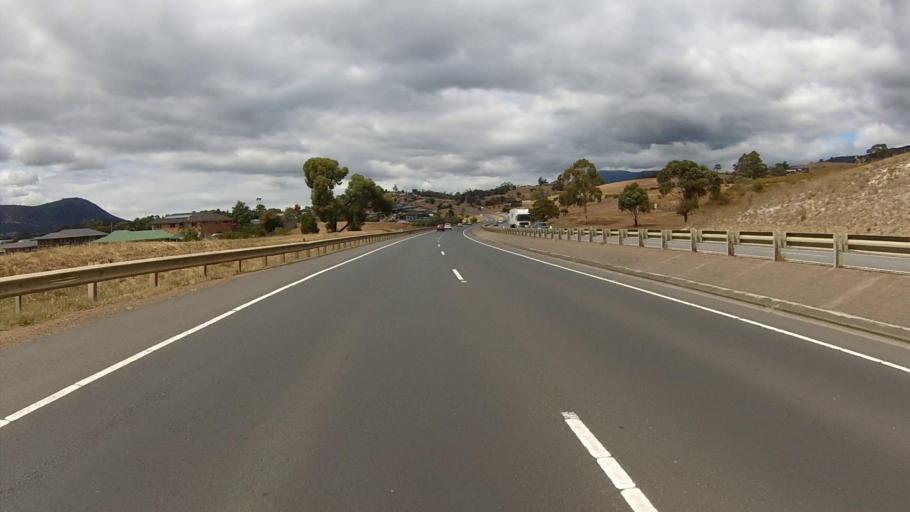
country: AU
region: Tasmania
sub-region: Glenorchy
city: Granton
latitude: -42.7625
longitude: 147.2345
